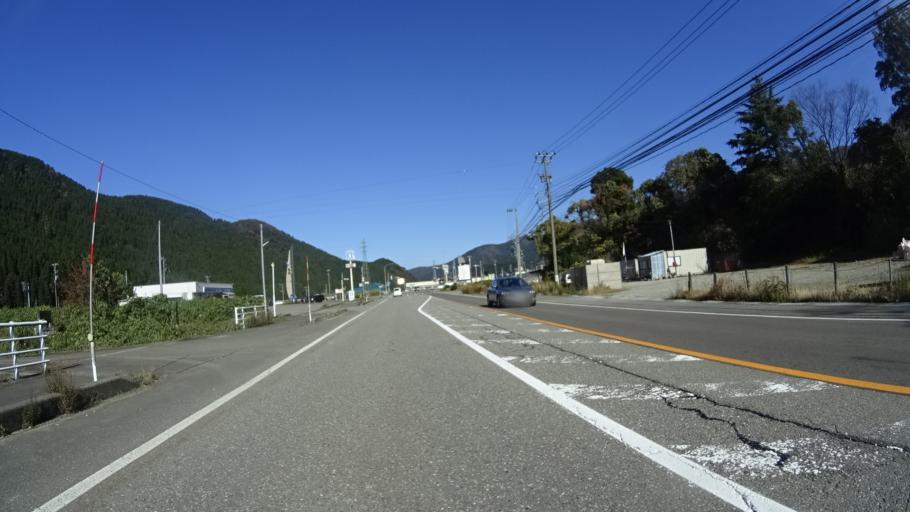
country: JP
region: Ishikawa
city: Tsurugi-asahimachi
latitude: 36.4219
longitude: 136.6312
